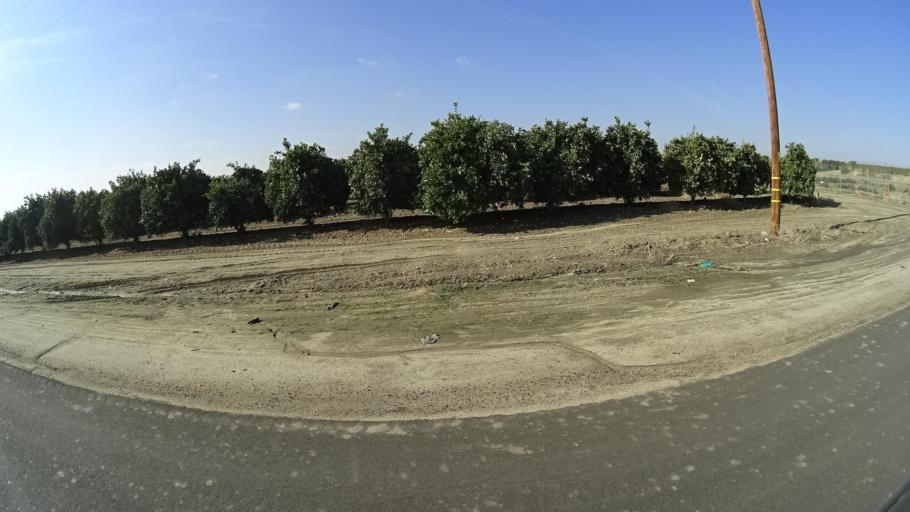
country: US
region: California
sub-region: Kern County
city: Arvin
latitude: 35.2737
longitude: -118.7707
